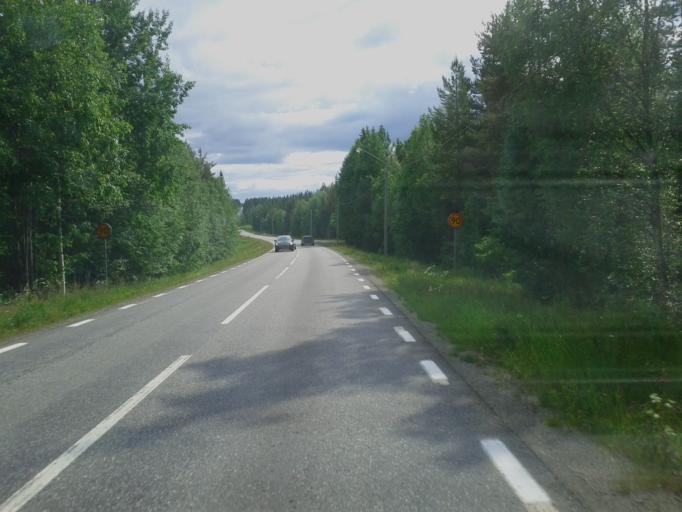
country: SE
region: Vaesterbotten
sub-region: Sorsele Kommun
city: Sorsele
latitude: 65.2391
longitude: 17.6604
